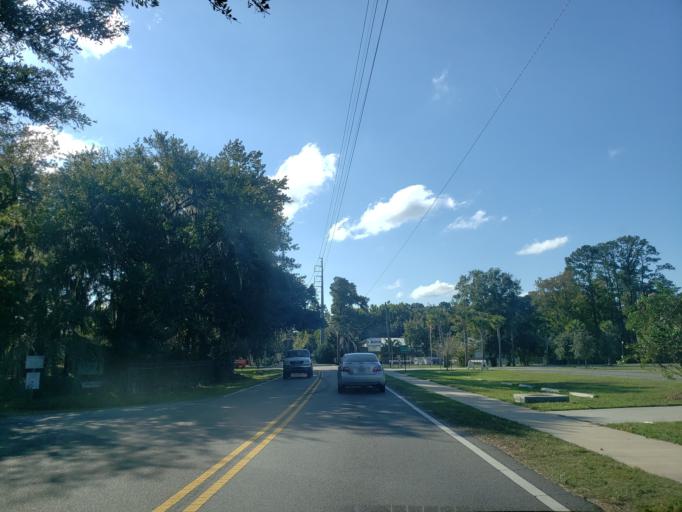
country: US
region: Georgia
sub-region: Chatham County
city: Isle of Hope
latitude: 31.9940
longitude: -81.0783
